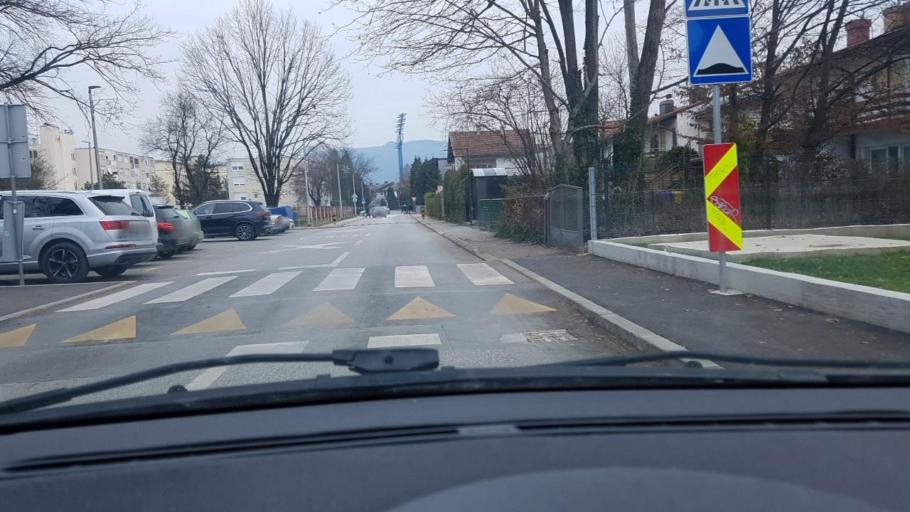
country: HR
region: Zagrebacka
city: Brdovec
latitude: 45.8655
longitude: 15.7950
